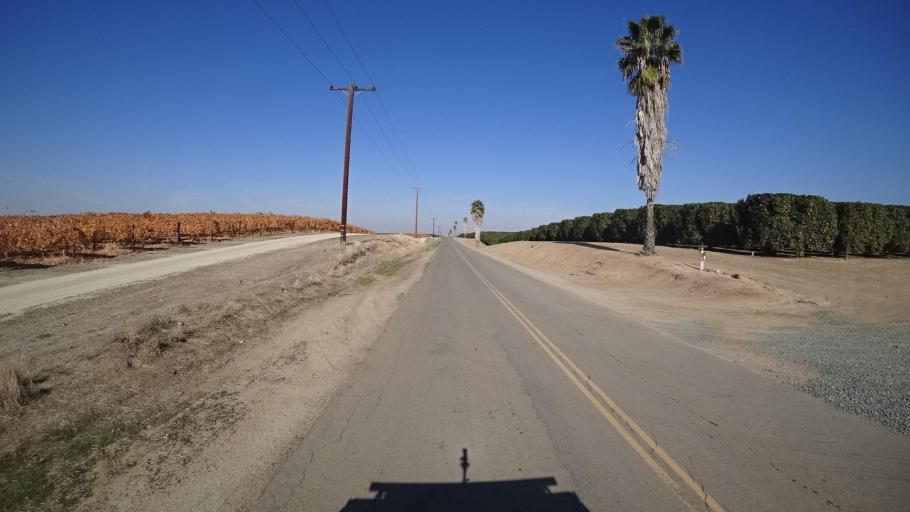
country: US
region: California
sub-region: Tulare County
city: Richgrove
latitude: 35.7071
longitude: -119.1338
